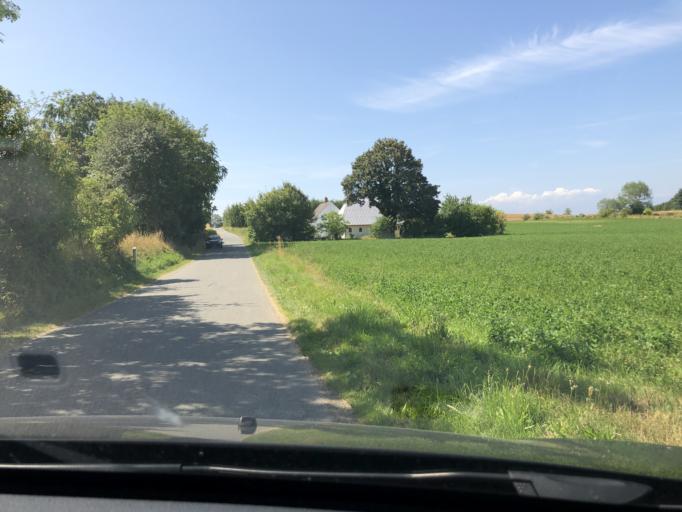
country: DK
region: South Denmark
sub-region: AEro Kommune
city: AEroskobing
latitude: 54.9300
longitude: 10.2855
